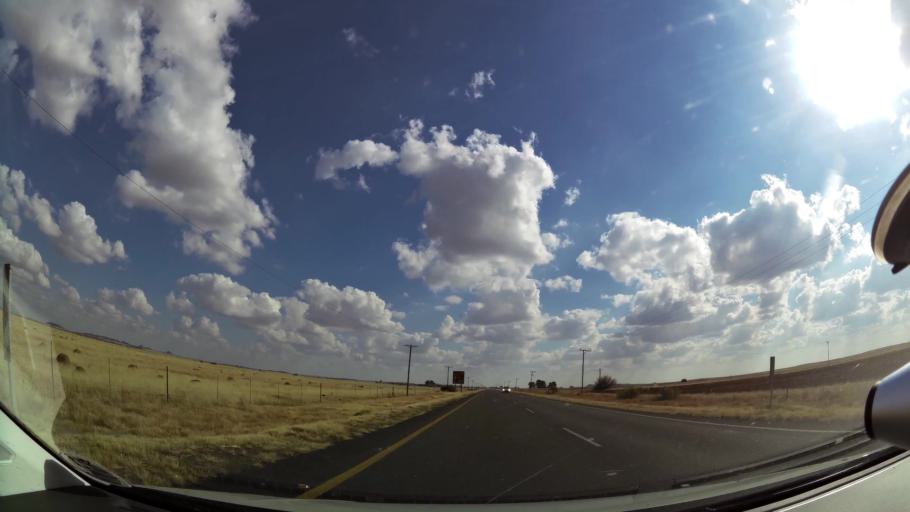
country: ZA
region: Orange Free State
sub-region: Xhariep District Municipality
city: Koffiefontein
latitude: -29.1297
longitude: 25.5105
